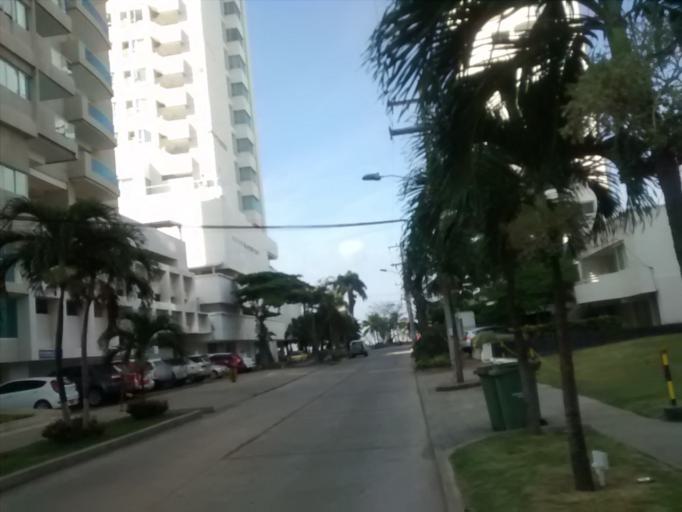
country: CO
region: Bolivar
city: Cartagena
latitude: 10.3965
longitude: -75.5549
